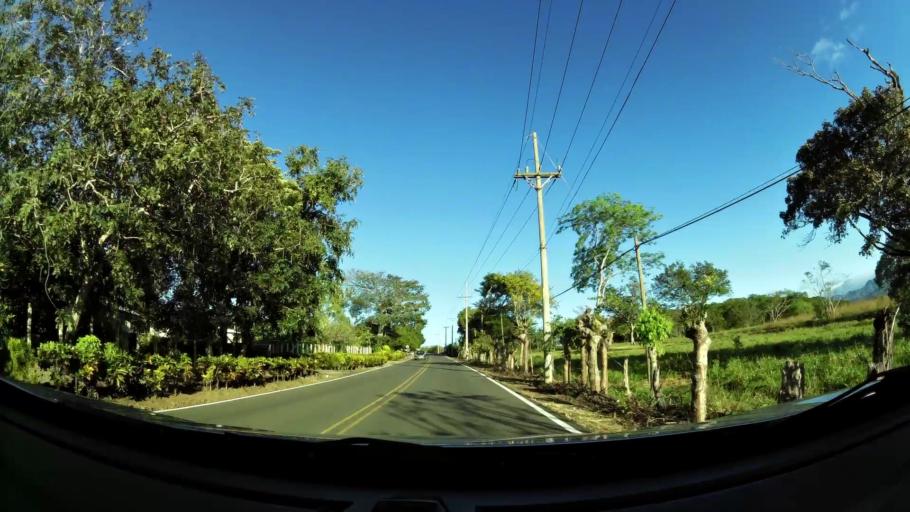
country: CR
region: Puntarenas
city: Miramar
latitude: 10.1071
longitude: -84.8246
